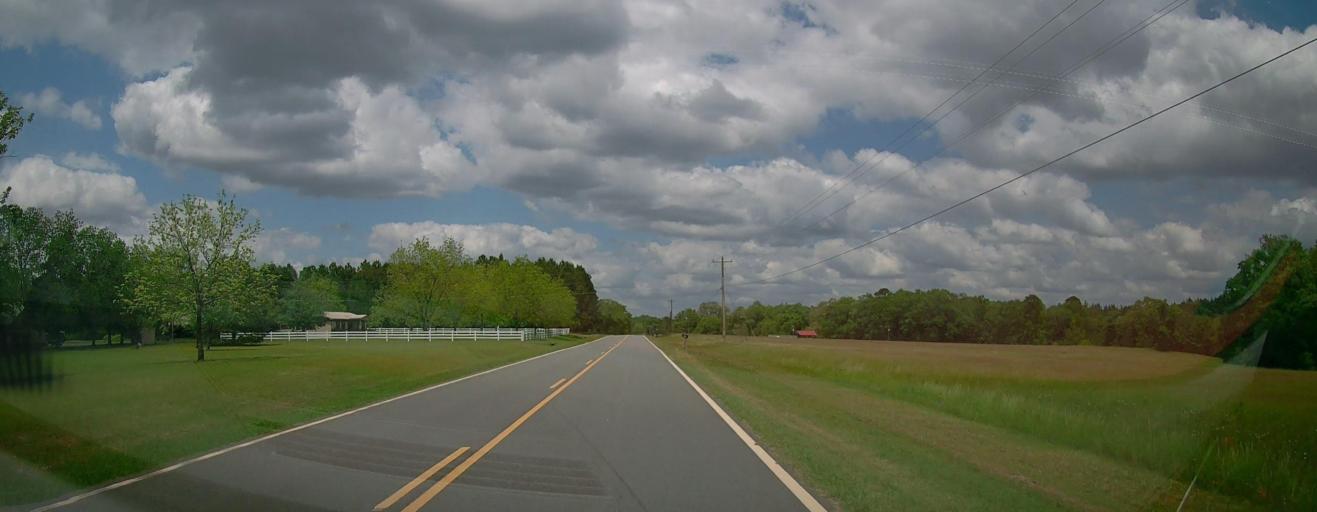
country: US
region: Georgia
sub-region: Laurens County
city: Dublin
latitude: 32.6134
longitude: -82.9680
